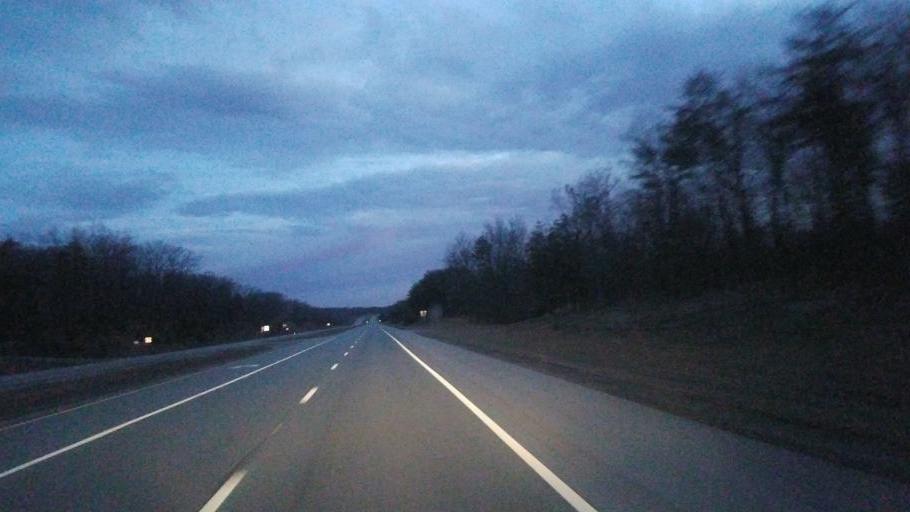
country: US
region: Tennessee
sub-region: Van Buren County
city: Spencer
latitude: 35.5660
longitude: -85.4712
